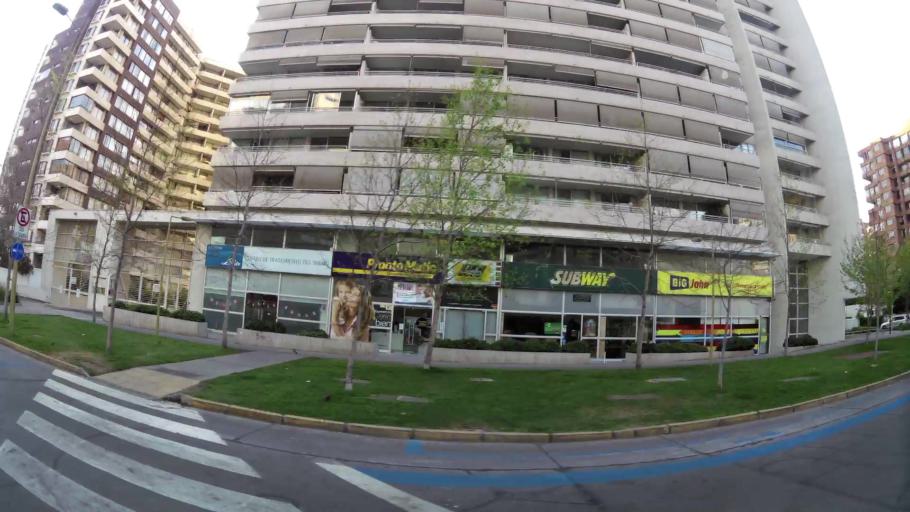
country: CL
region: Santiago Metropolitan
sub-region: Provincia de Santiago
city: Villa Presidente Frei, Nunoa, Santiago, Chile
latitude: -33.4075
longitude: -70.5649
